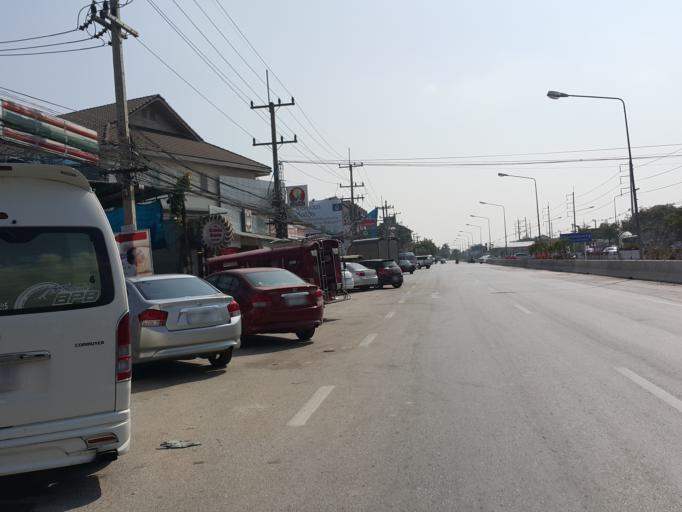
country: TH
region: Chiang Mai
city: Chiang Mai
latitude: 18.7486
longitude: 98.9413
